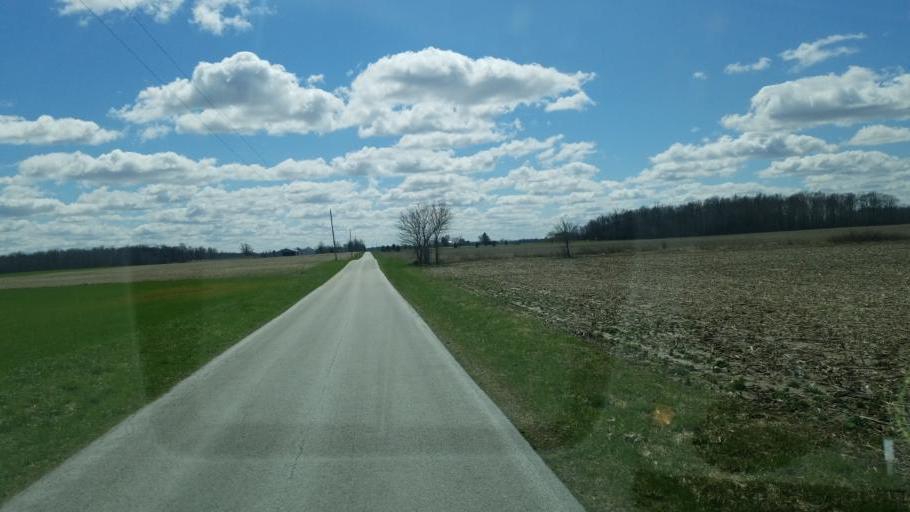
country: US
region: Ohio
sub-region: Hancock County
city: Arlington
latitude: 40.9281
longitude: -83.5369
